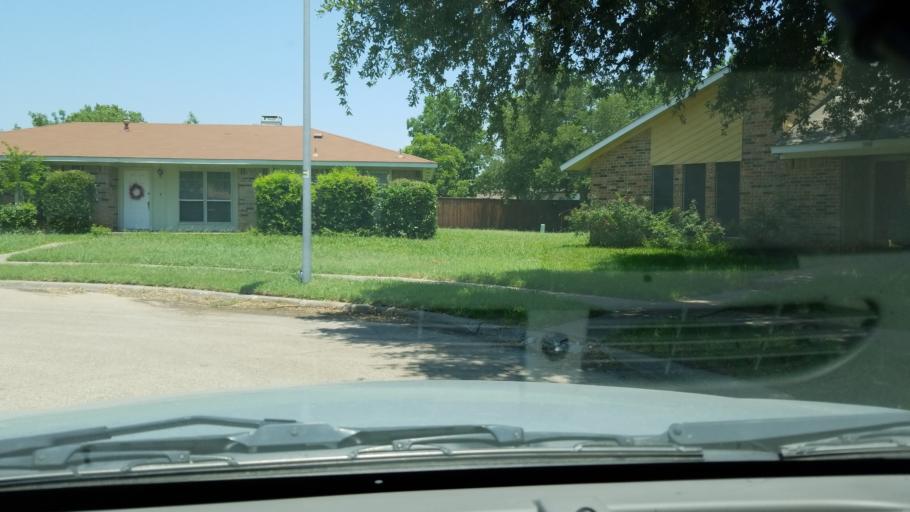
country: US
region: Texas
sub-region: Dallas County
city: Coppell
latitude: 32.9623
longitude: -96.9901
